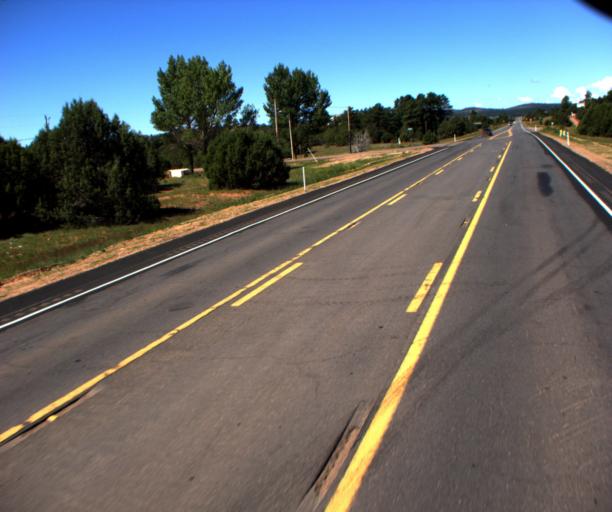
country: US
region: Arizona
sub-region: Navajo County
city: Linden
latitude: 34.2854
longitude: -110.1274
